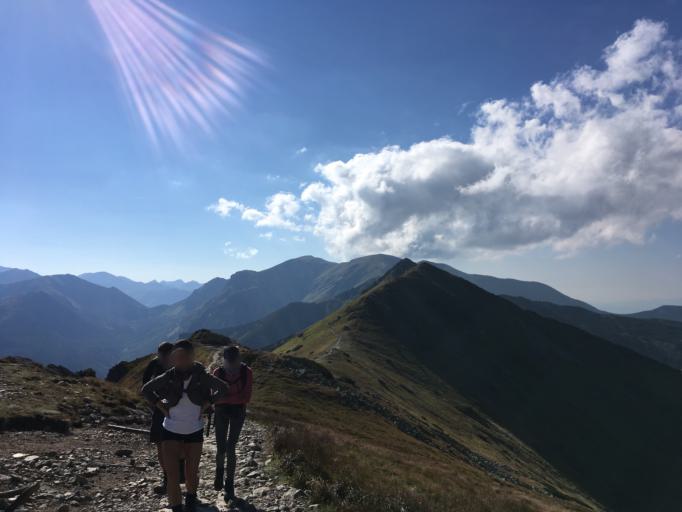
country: PL
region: Lesser Poland Voivodeship
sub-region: Powiat tatrzanski
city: Zakopane
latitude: 49.2301
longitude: 19.9736
